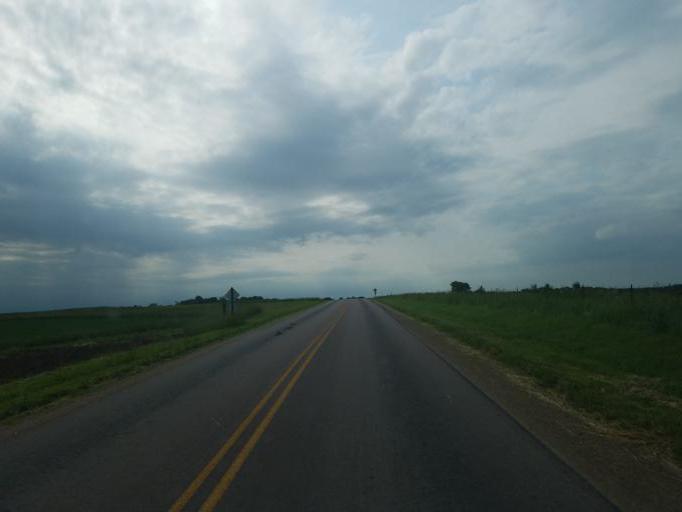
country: US
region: Wisconsin
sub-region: Vernon County
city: Hillsboro
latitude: 43.6051
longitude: -90.4275
